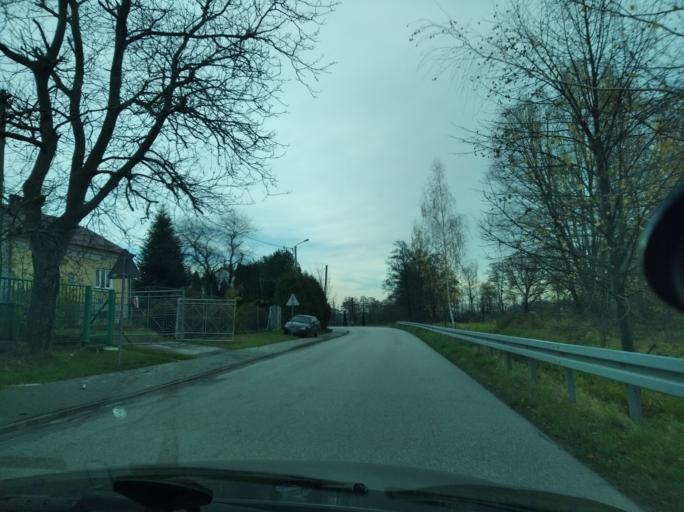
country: PL
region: Subcarpathian Voivodeship
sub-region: Powiat lancucki
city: Albigowa
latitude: 50.0357
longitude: 22.2093
